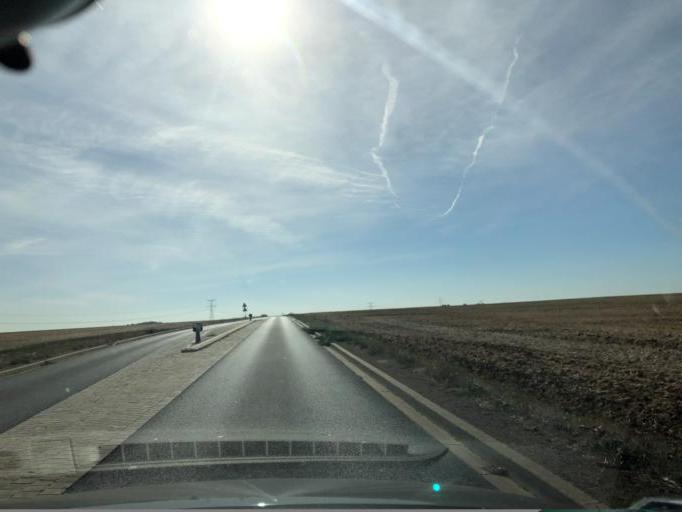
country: FR
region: Ile-de-France
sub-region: Departement de l'Essonne
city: Maisse
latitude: 48.3431
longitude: 2.3266
